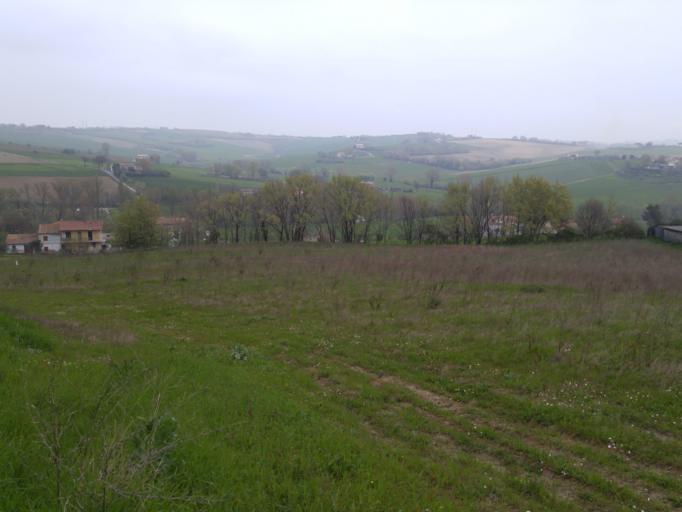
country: IT
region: The Marches
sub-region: Provincia di Pesaro e Urbino
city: Calcinelli
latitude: 43.7730
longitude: 12.9159
